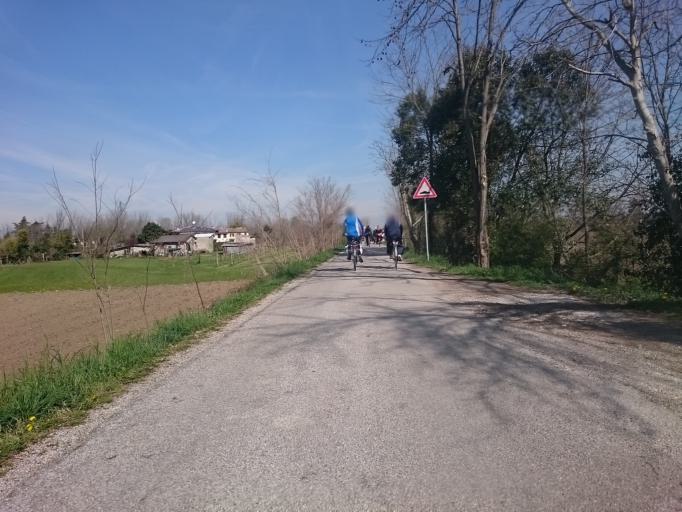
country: IT
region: Veneto
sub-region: Provincia di Padova
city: Sarmeola
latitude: 45.4276
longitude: 11.8291
